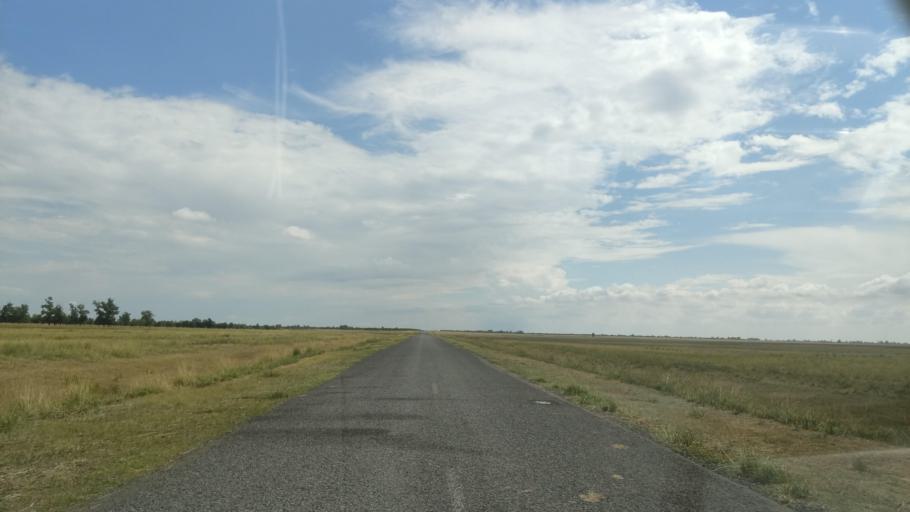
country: KZ
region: Pavlodar
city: Pavlodar
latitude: 52.6358
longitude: 76.9322
